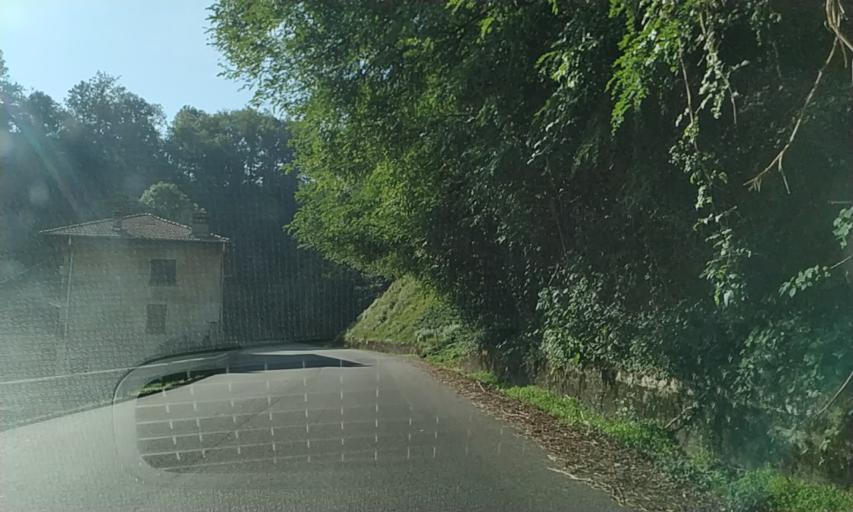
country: IT
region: Piedmont
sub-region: Provincia di Biella
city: Coggiola
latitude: 45.6822
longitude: 8.1809
